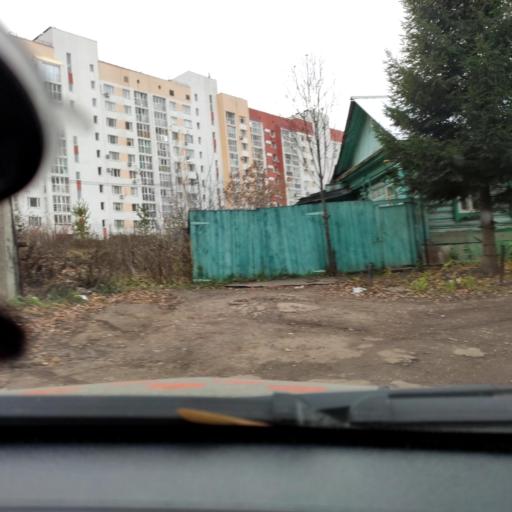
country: RU
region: Bashkortostan
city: Ufa
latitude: 54.7168
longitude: 55.9769
